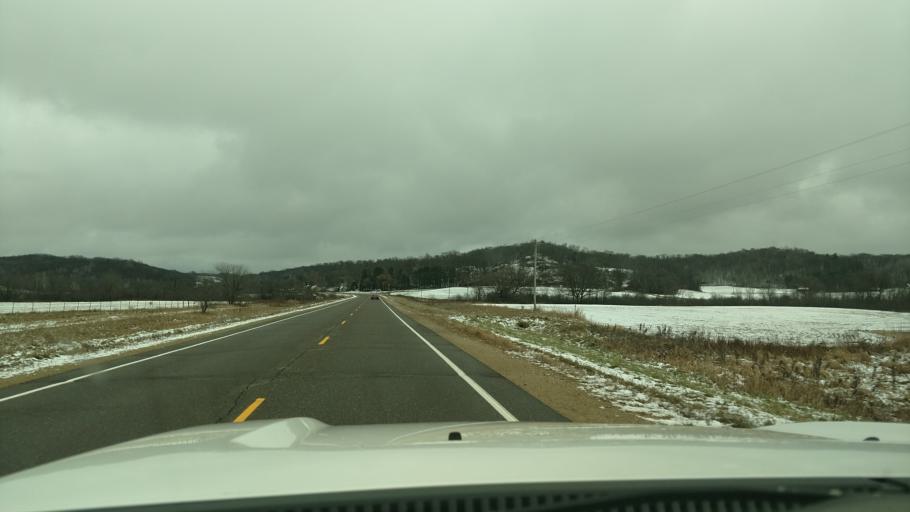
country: US
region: Wisconsin
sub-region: Dunn County
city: Tainter Lake
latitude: 45.1258
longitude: -91.8538
